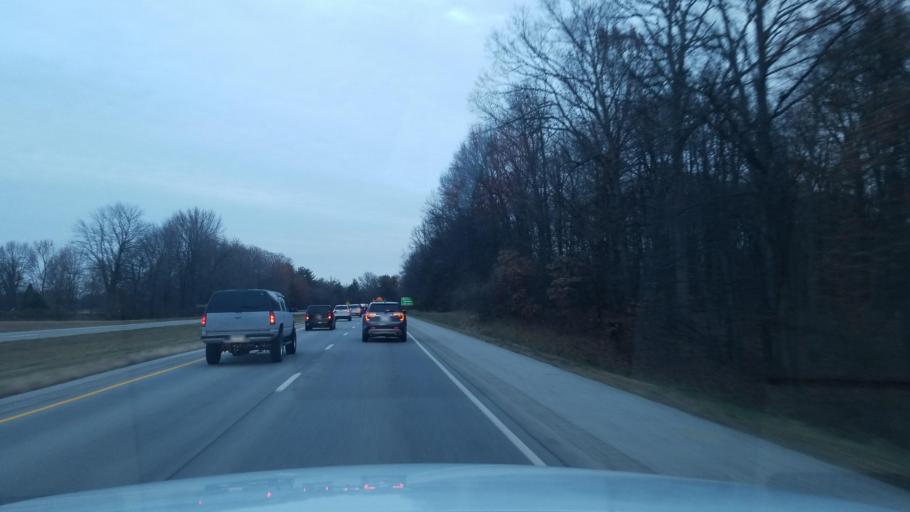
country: US
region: Indiana
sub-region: Vanderburgh County
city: Evansville
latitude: 37.9608
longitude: -87.6911
